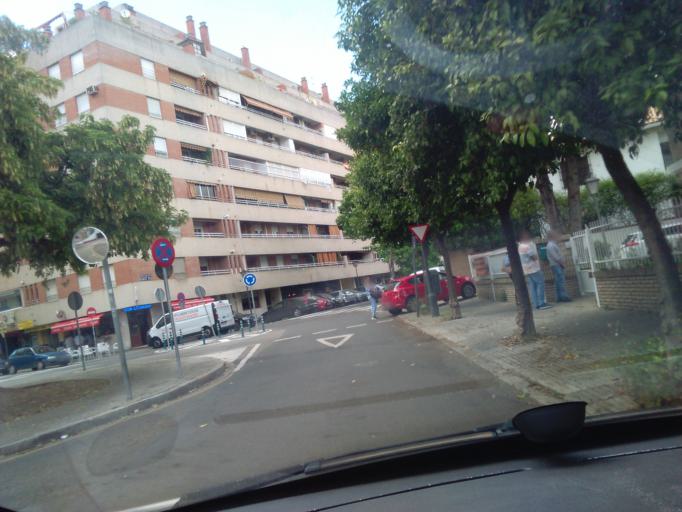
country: ES
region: Andalusia
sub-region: Provincia de Sevilla
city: Sevilla
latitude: 37.3620
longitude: -5.9852
